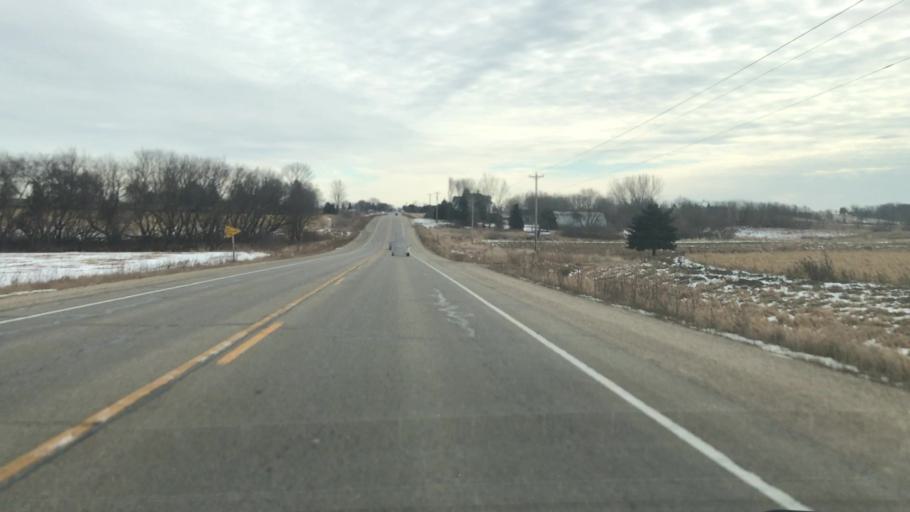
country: US
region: Wisconsin
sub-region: Dodge County
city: Theresa
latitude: 43.4282
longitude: -88.4358
